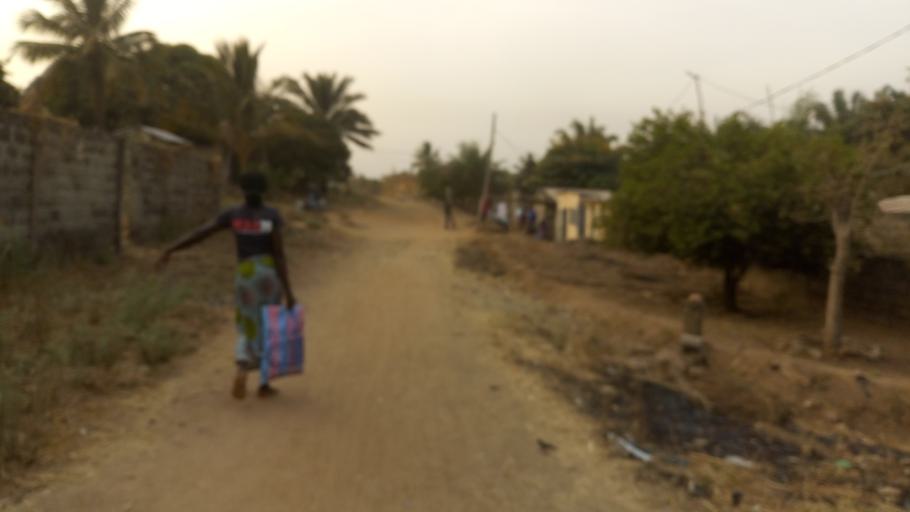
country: TG
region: Kara
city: Kara
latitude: 9.5608
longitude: 1.2082
